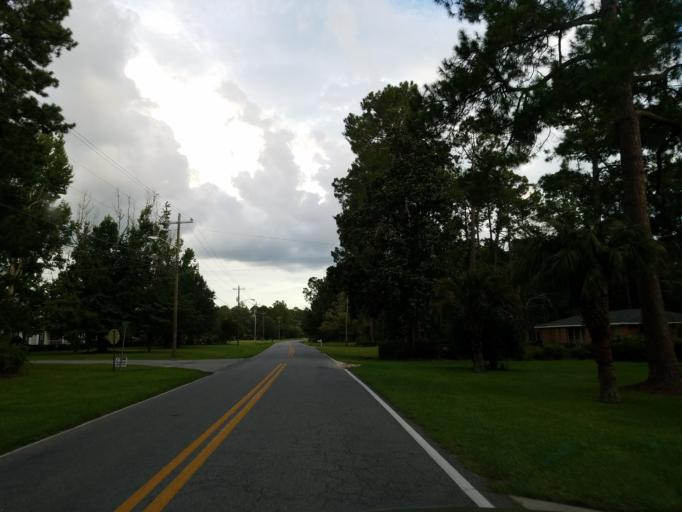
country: US
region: Georgia
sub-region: Cook County
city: Adel
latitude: 31.1464
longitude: -83.4173
